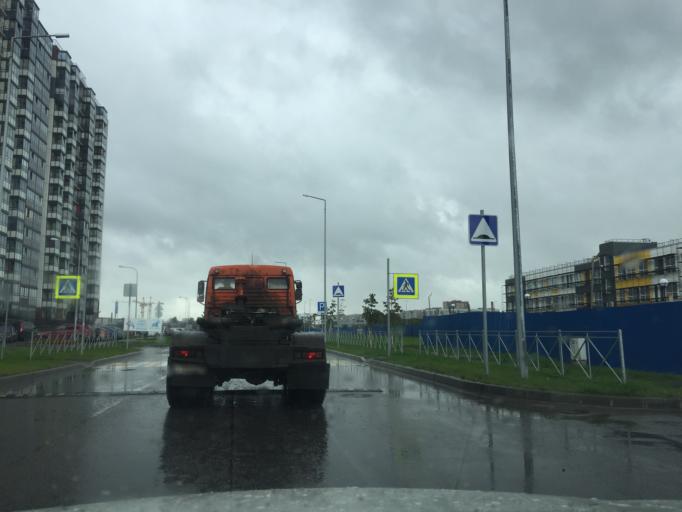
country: RU
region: St.-Petersburg
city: Sosnovaya Polyana
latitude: 59.7933
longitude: 30.1656
